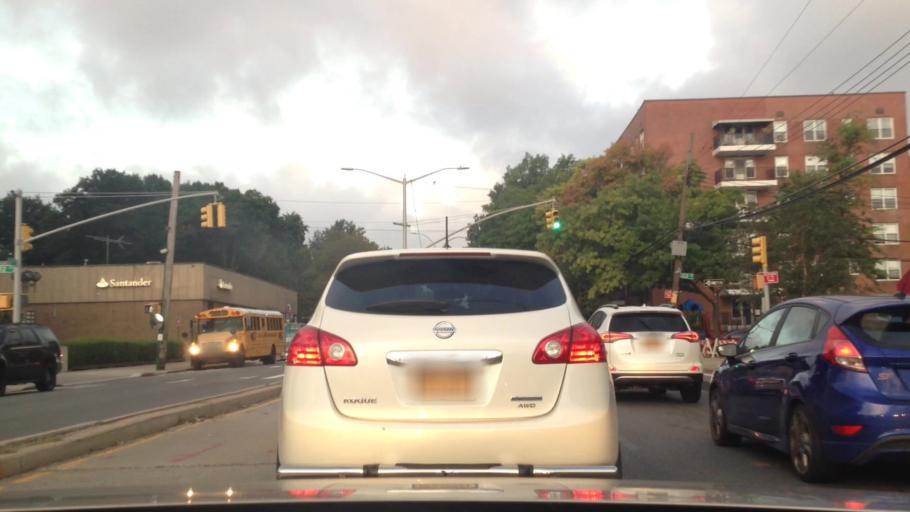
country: US
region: New York
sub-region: Queens County
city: Jamaica
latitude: 40.7195
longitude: -73.8109
